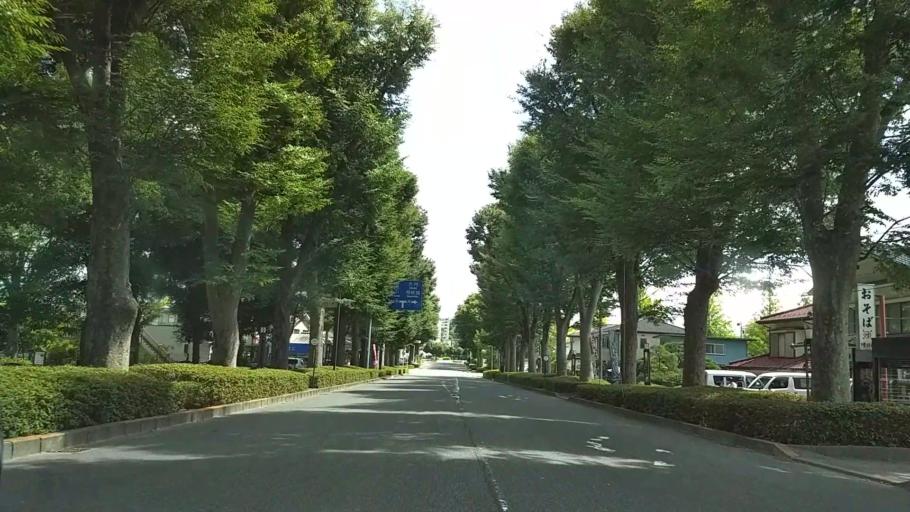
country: JP
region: Tokyo
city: Hachioji
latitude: 35.6485
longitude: 139.2919
